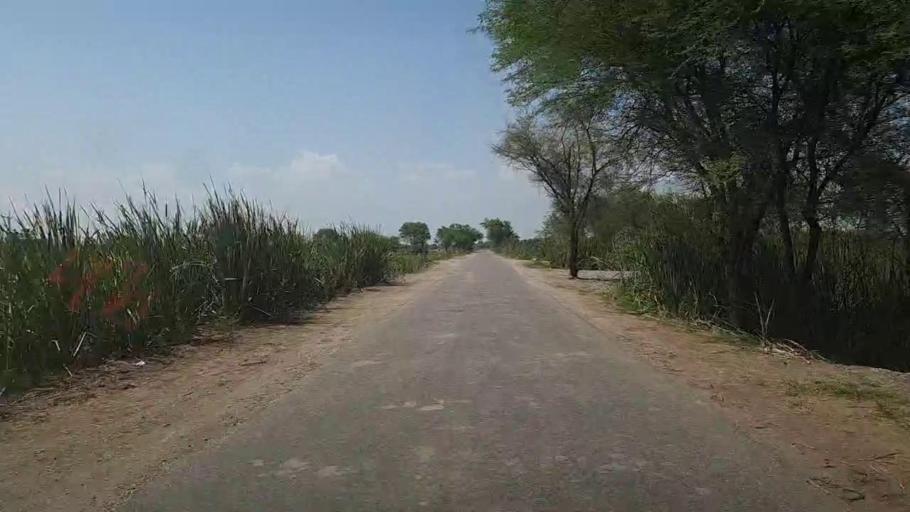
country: PK
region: Sindh
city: Khairpur
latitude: 28.0738
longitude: 69.6400
